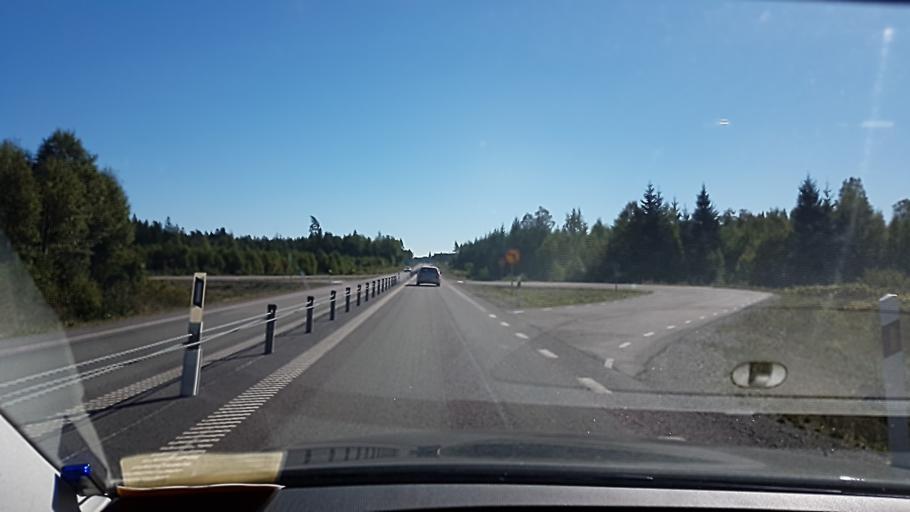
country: SE
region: Kalmar
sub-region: Emmaboda Kommun
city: Emmaboda
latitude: 56.7318
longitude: 15.5426
